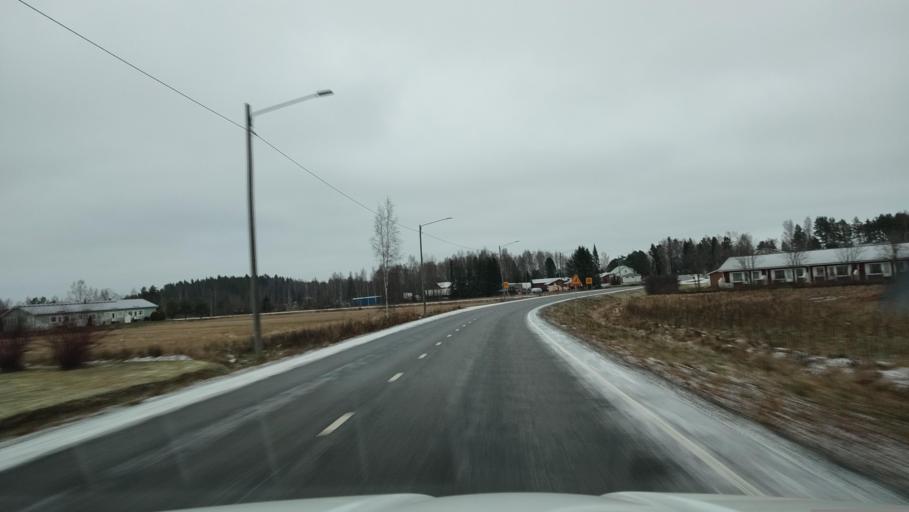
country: FI
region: Southern Ostrobothnia
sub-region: Suupohja
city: Karijoki
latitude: 62.3049
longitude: 21.6939
